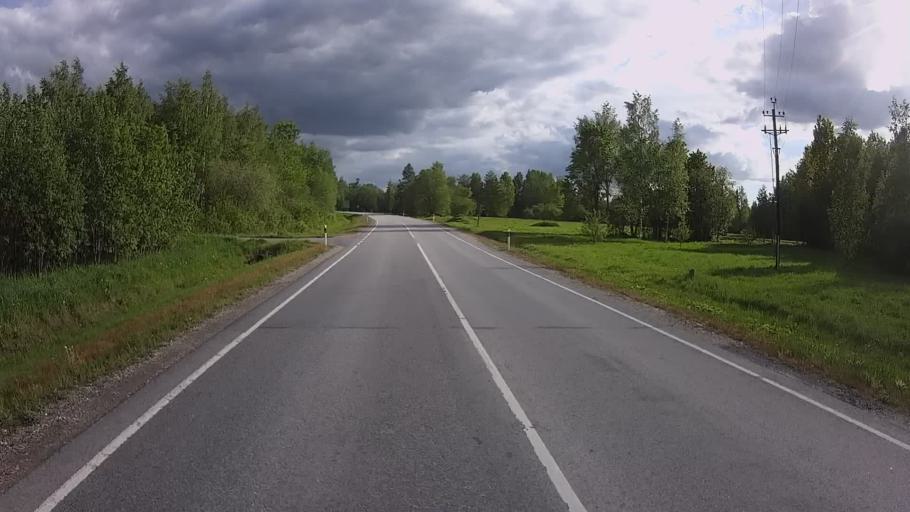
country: EE
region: Jogevamaa
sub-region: Mustvee linn
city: Mustvee
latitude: 58.9783
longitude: 26.8287
